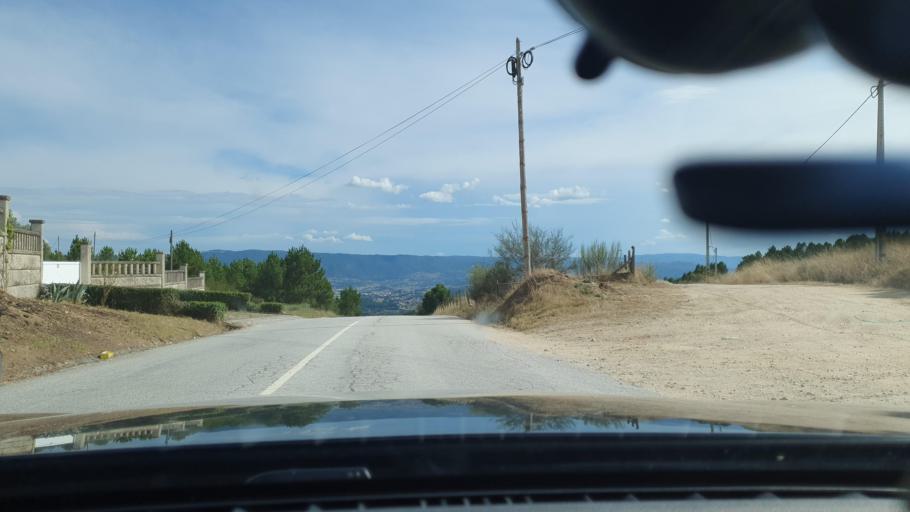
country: PT
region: Vila Real
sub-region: Chaves
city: Chaves
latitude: 41.7954
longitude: -7.5137
